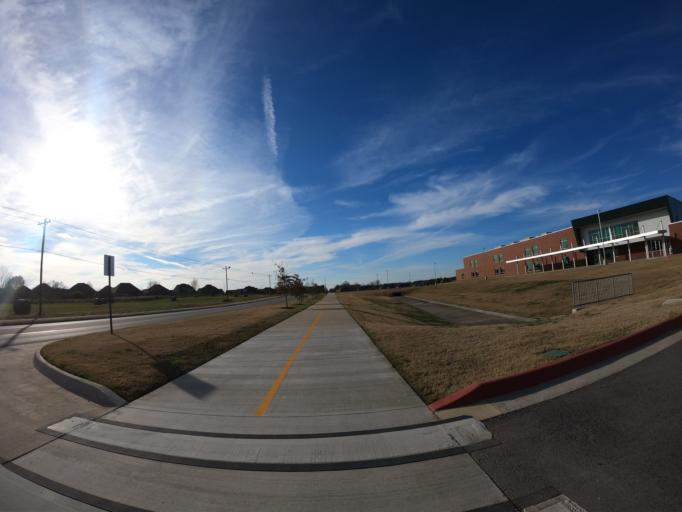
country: US
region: Arkansas
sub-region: Benton County
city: Lowell
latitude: 36.2692
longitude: -94.1643
